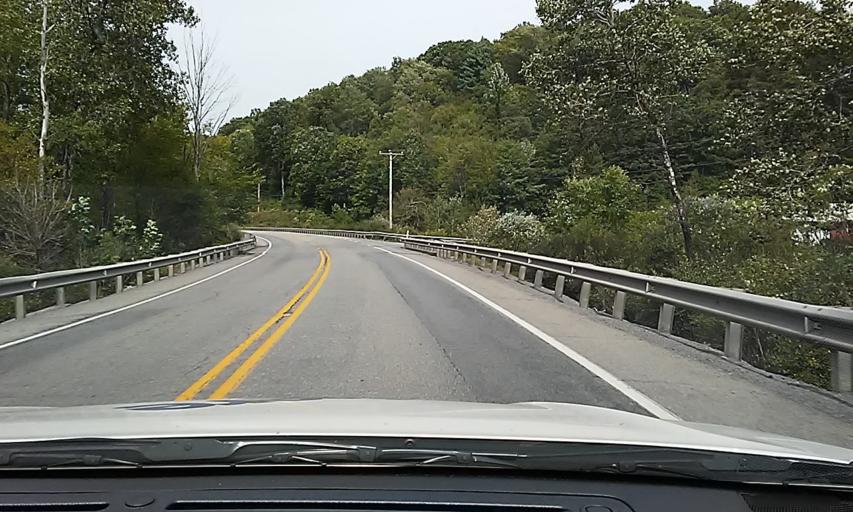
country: US
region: Pennsylvania
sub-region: Clearfield County
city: Treasure Lake
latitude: 41.2211
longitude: -78.5889
